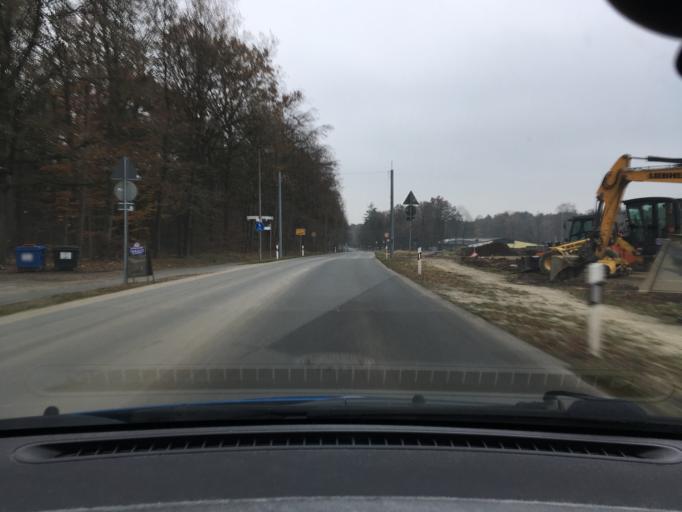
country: DE
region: Lower Saxony
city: Soltau
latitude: 52.9950
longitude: 9.8511
